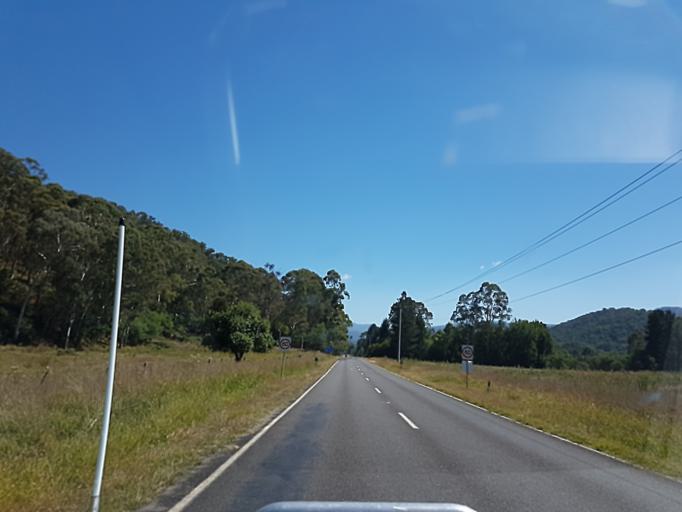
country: AU
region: Victoria
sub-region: Alpine
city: Mount Beauty
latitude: -36.7809
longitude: 147.0347
